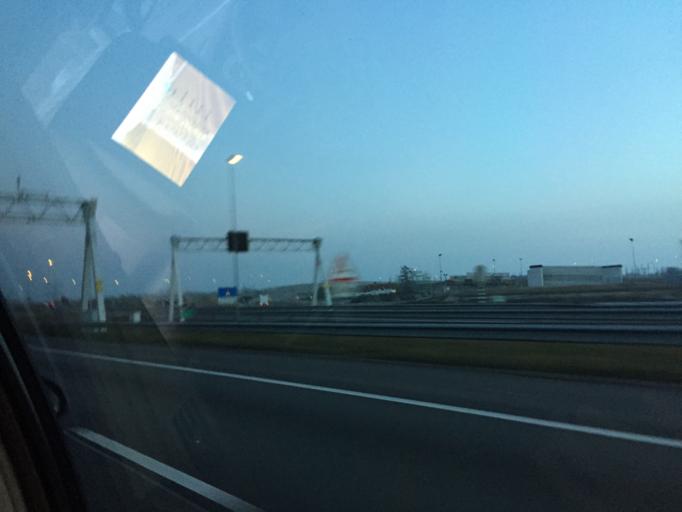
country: NL
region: North Holland
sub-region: Gemeente Naarden
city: Naarden
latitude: 52.3119
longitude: 5.1157
